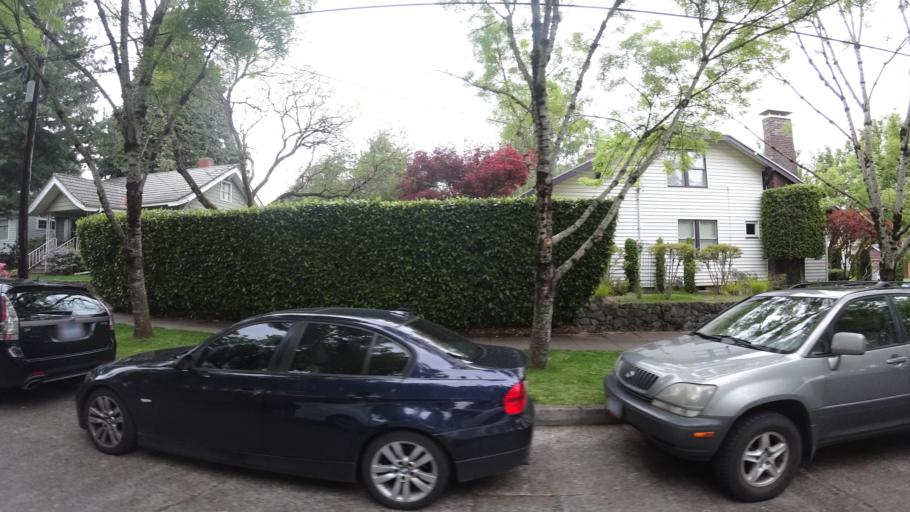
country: US
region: Oregon
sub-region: Clackamas County
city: Milwaukie
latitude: 45.4751
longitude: -122.6504
